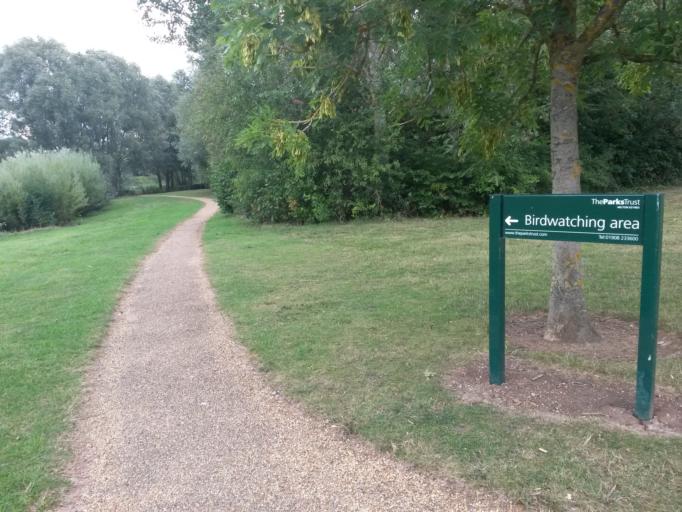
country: GB
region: England
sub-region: Milton Keynes
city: Simpson
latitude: 52.0019
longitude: -0.7070
